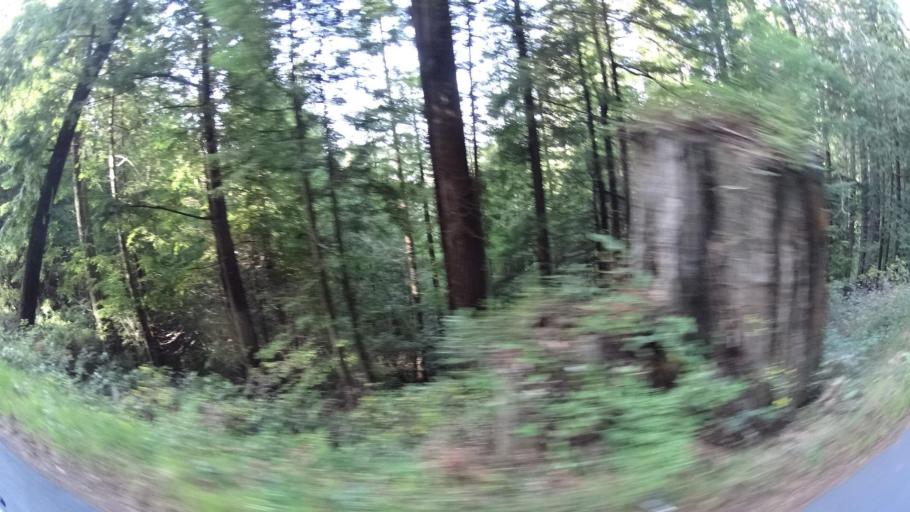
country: US
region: California
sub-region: Humboldt County
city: Bayside
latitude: 40.7566
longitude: -124.0348
